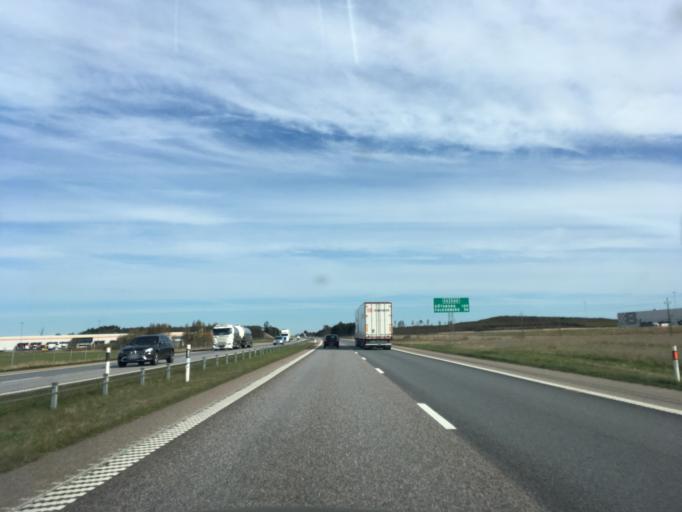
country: SE
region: Halland
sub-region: Halmstads Kommun
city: Halmstad
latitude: 56.7170
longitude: 12.8868
